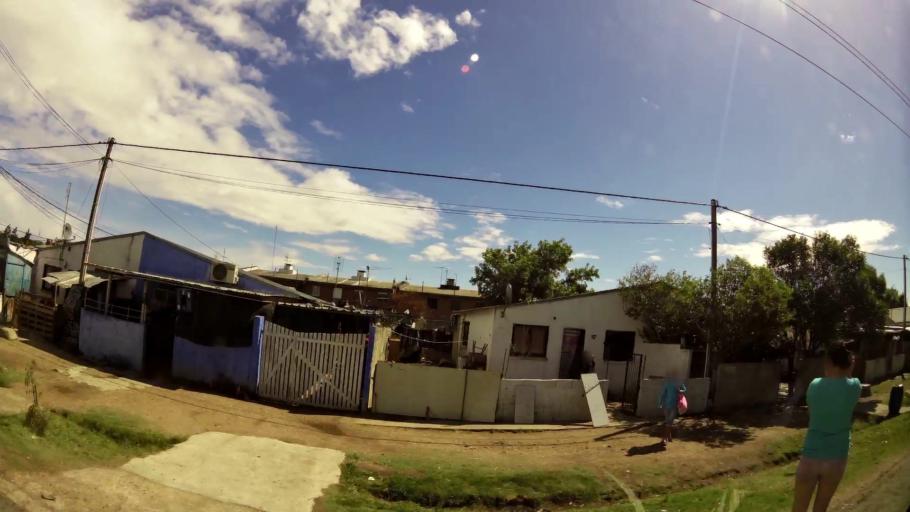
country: UY
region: Montevideo
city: Montevideo
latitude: -34.8443
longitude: -56.1900
